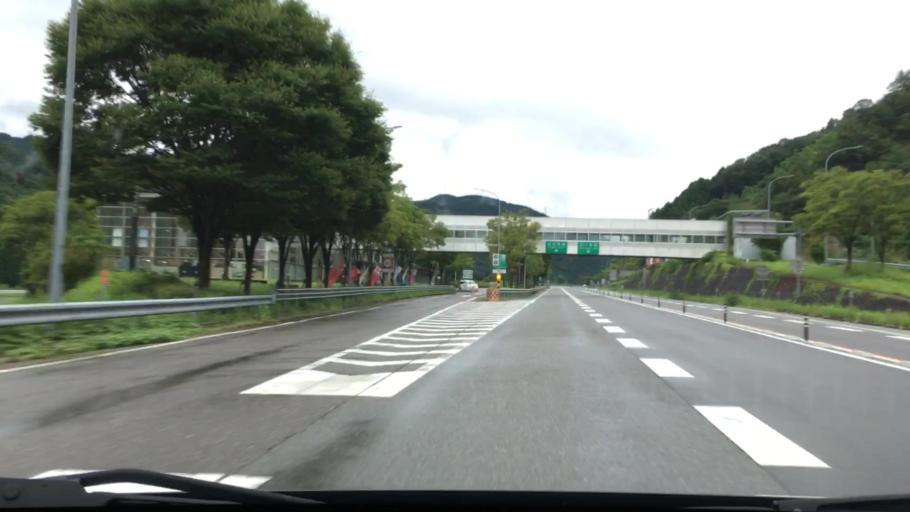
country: JP
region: Hyogo
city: Nishiwaki
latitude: 35.2143
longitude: 134.7938
